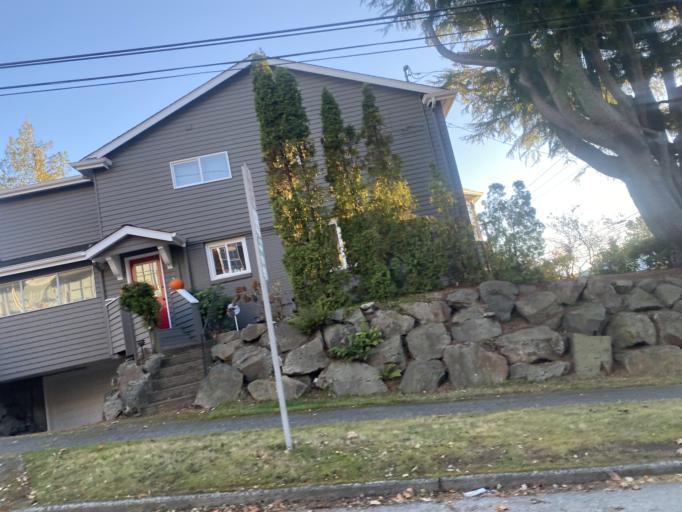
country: US
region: Washington
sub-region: King County
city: Seattle
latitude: 47.6400
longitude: -122.3927
